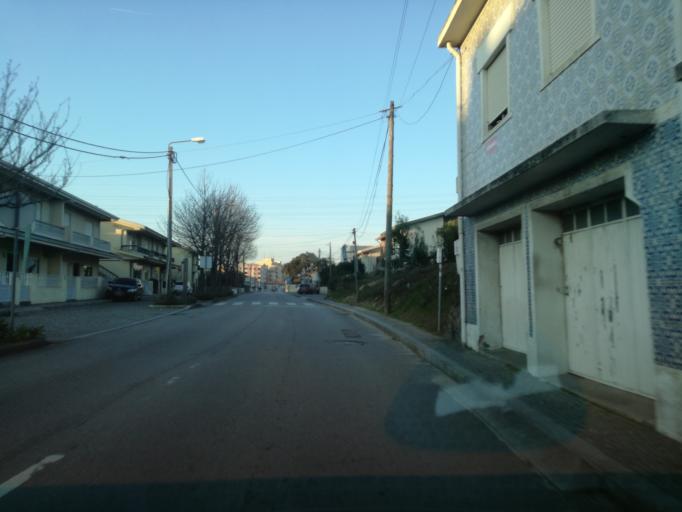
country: PT
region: Porto
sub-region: Maia
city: Milheiros
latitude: 41.2258
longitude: -8.5890
